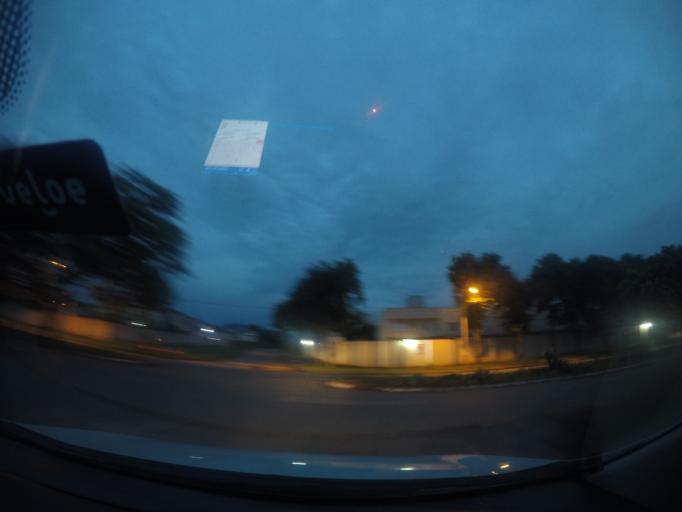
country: BR
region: Goias
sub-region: Goiania
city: Goiania
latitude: -16.6451
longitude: -49.2371
